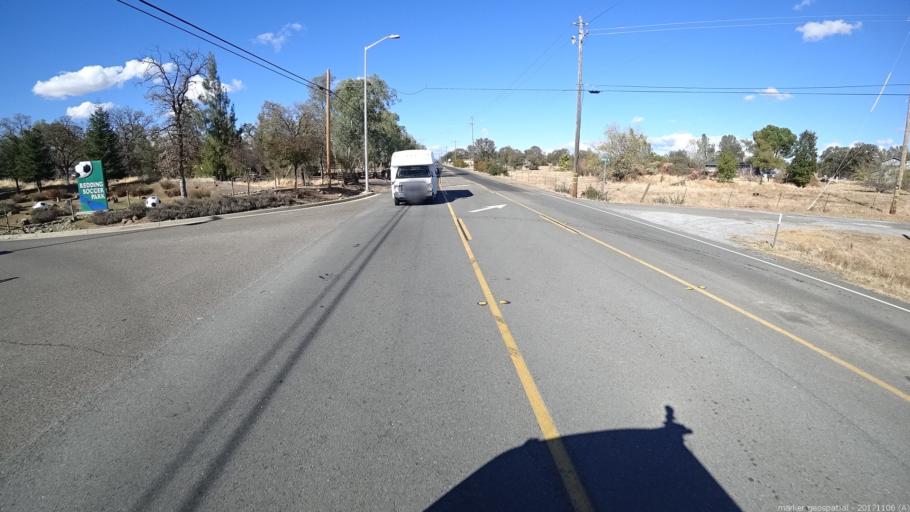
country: US
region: California
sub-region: Shasta County
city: Palo Cedro
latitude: 40.5745
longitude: -122.3029
